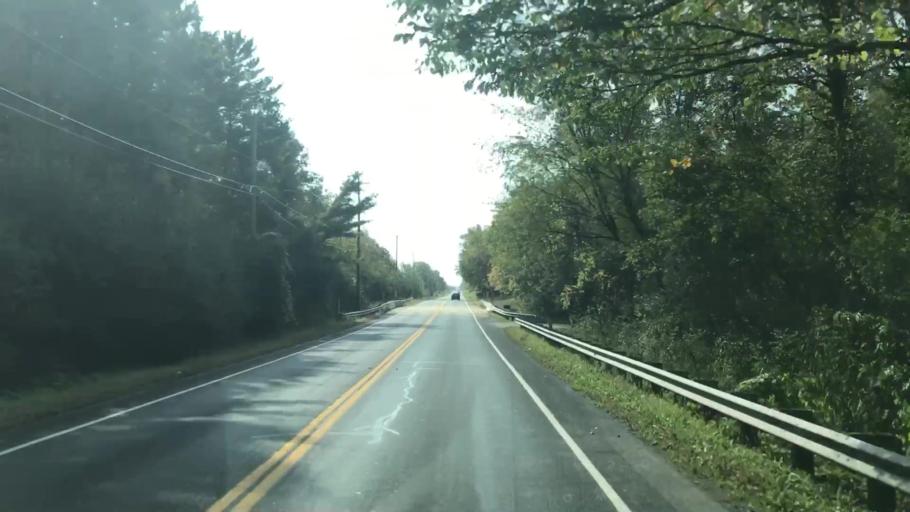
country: US
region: Wisconsin
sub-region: Ozaukee County
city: Mequon
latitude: 43.2194
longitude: -88.0435
